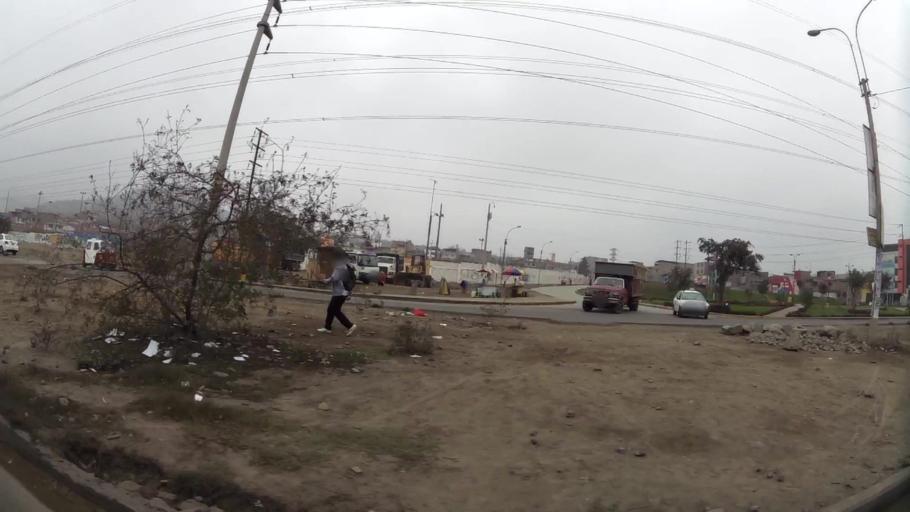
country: PE
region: Lima
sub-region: Lima
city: Surco
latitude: -12.1927
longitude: -76.9364
